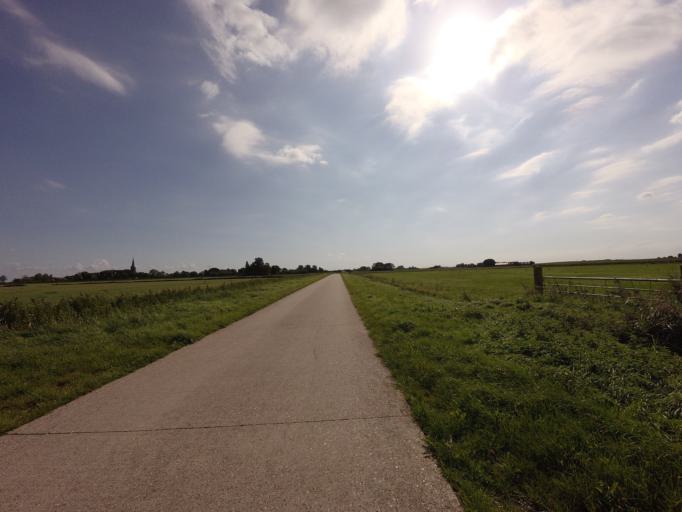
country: NL
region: Friesland
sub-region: Gemeente Littenseradiel
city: Makkum
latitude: 53.0811
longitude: 5.6317
